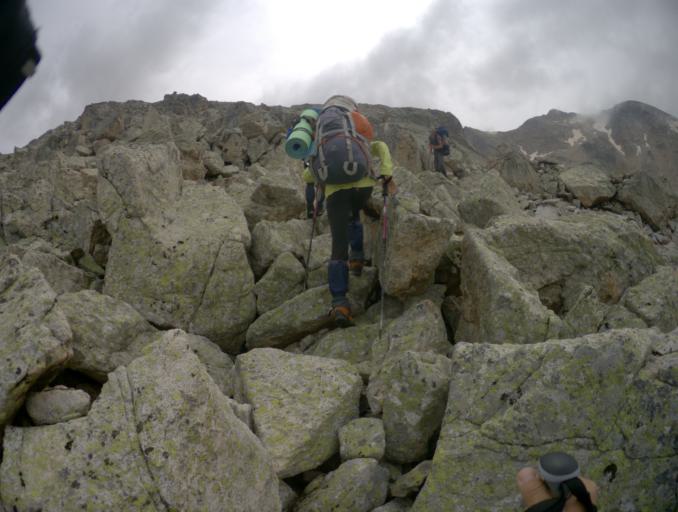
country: RU
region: Karachayevo-Cherkesiya
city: Uchkulan
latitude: 43.2852
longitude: 42.1017
